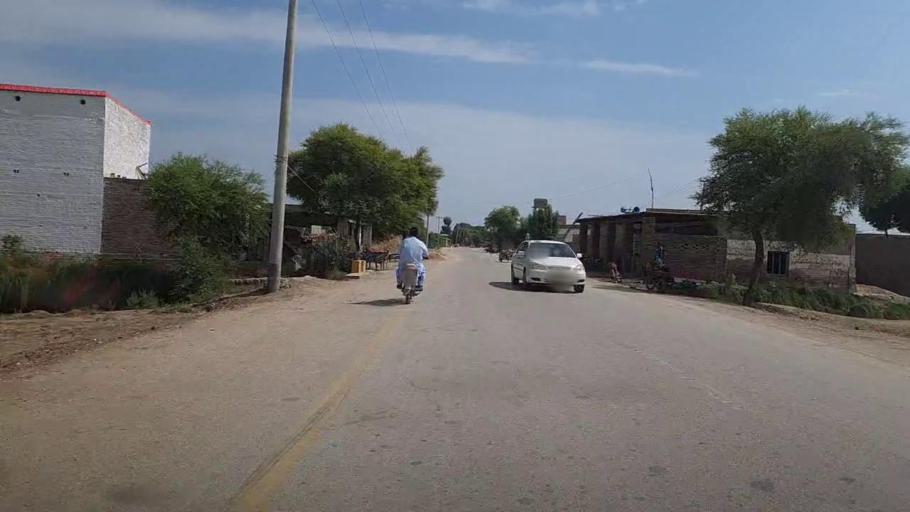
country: PK
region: Sindh
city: Thul
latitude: 28.2409
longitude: 68.7881
